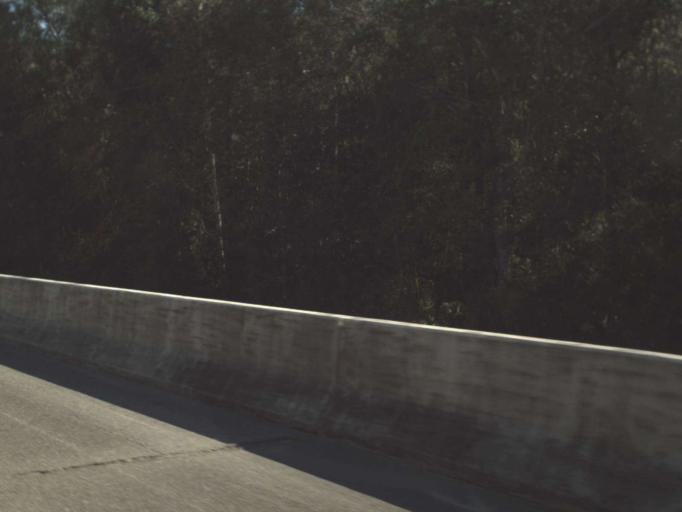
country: US
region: Florida
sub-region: Walton County
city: Freeport
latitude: 30.5386
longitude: -85.9204
